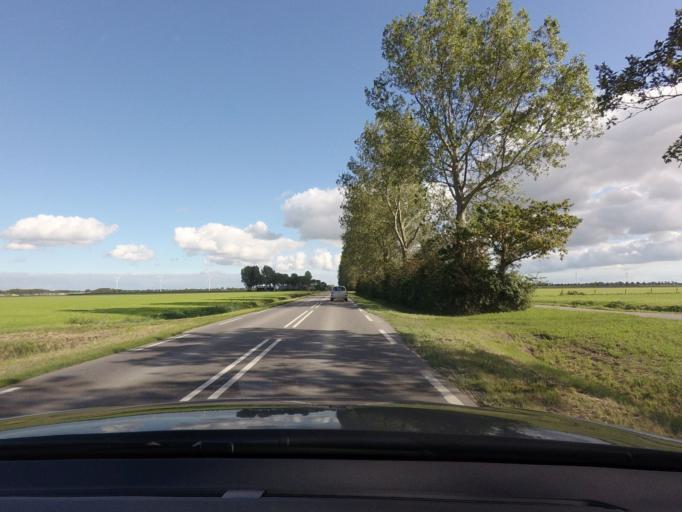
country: NL
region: North Holland
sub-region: Gemeente Schagen
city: Harenkarspel
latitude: 52.7214
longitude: 4.7507
